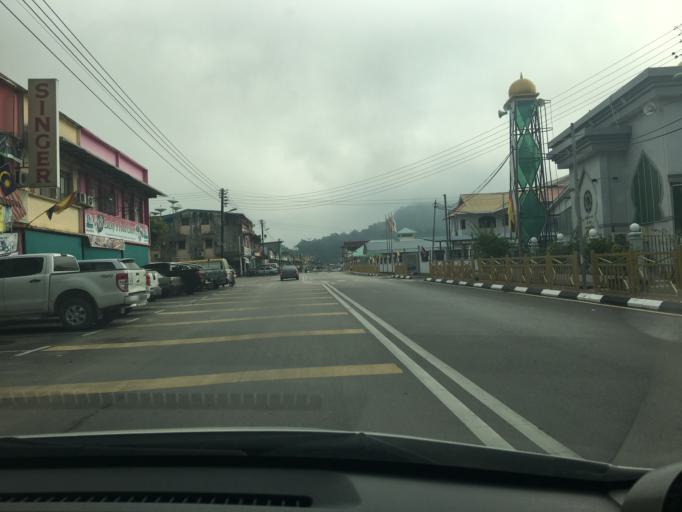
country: MY
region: Sarawak
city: Kuching
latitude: 1.4141
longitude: 110.1547
